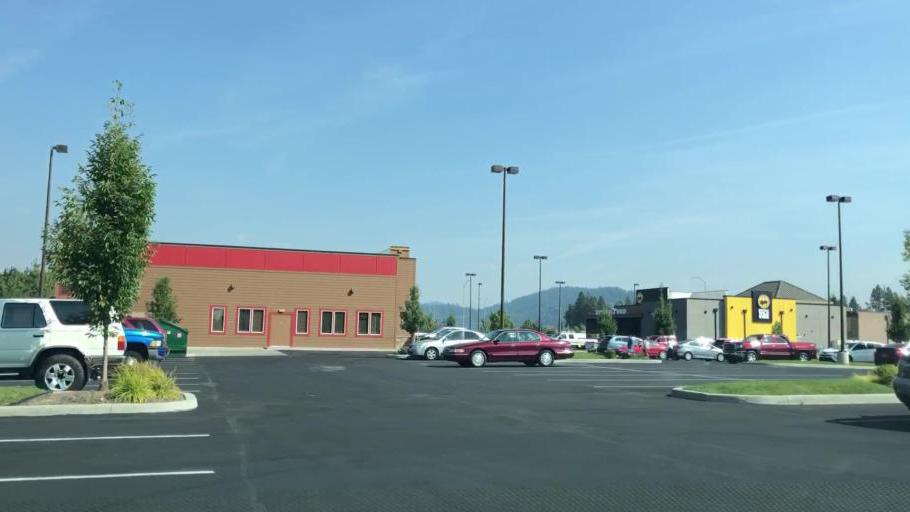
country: US
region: Idaho
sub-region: Kootenai County
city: Dalton Gardens
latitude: 47.7089
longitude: -116.7940
